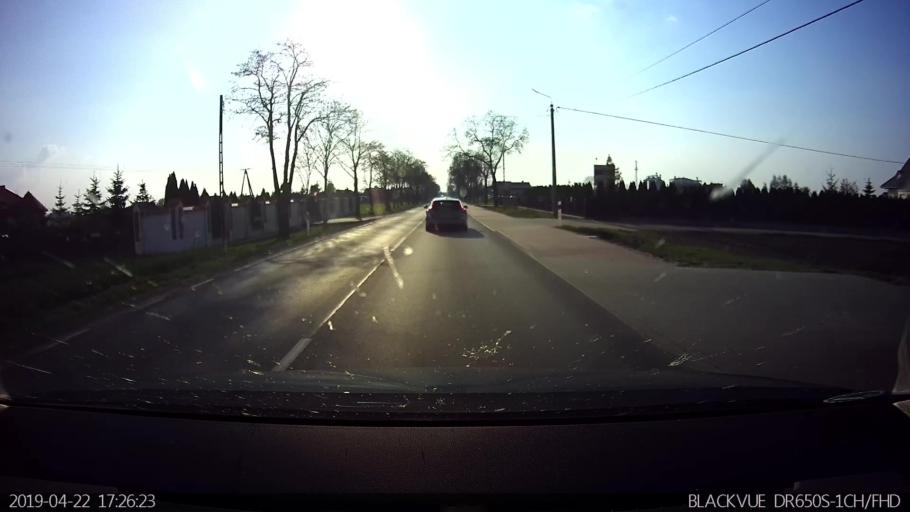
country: PL
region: Masovian Voivodeship
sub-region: Powiat sokolowski
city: Sokolow Podlaski
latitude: 52.3950
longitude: 22.2775
